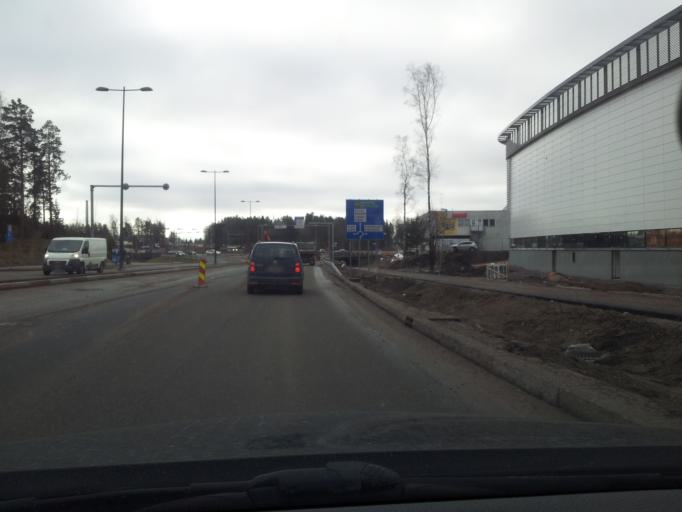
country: FI
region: Uusimaa
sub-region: Helsinki
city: Kauniainen
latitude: 60.1639
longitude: 24.7031
